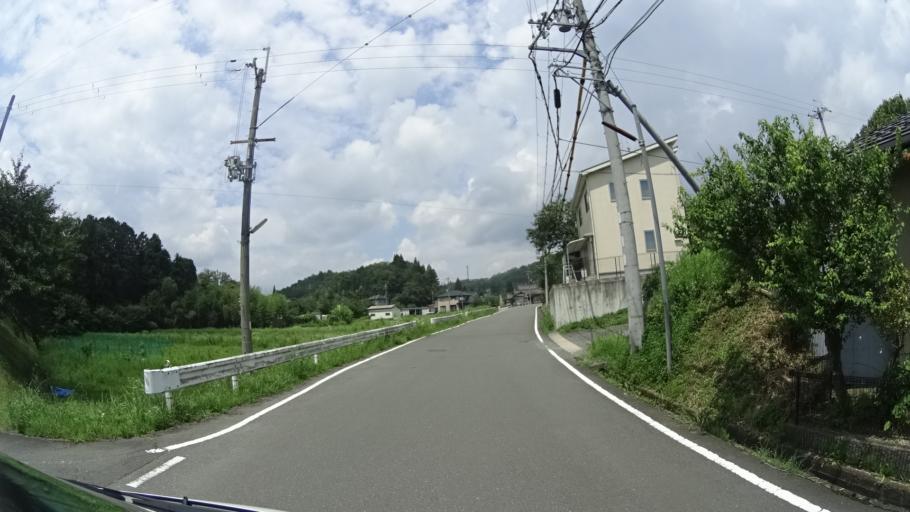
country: JP
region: Kyoto
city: Ayabe
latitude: 35.1782
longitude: 135.3616
